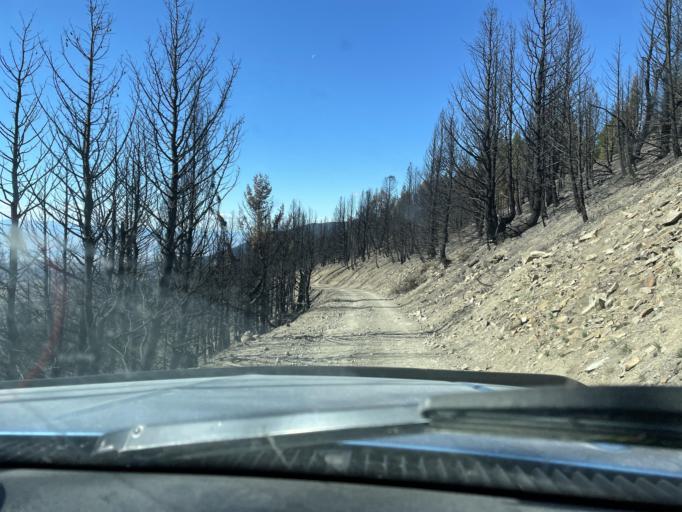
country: US
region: Montana
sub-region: Broadwater County
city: Townsend
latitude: 46.5013
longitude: -111.2725
